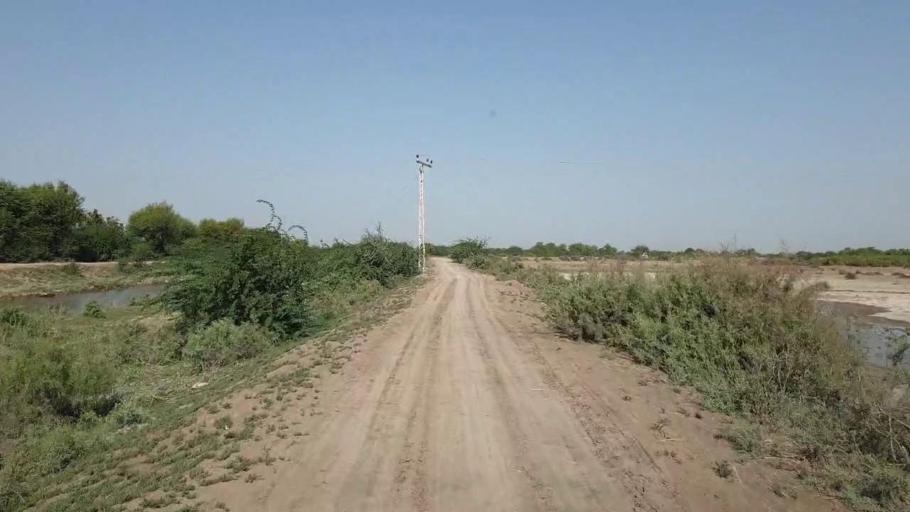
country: PK
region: Sindh
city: Tando Bago
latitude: 24.6624
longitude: 69.0678
